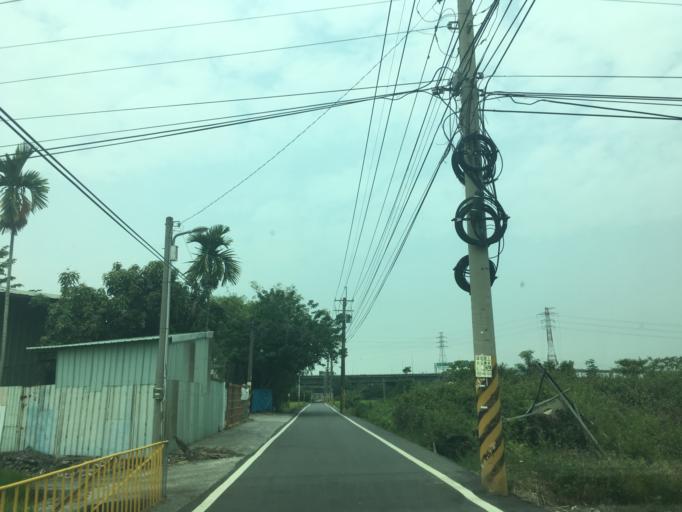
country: TW
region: Taiwan
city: Zhongxing New Village
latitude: 24.0422
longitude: 120.6807
